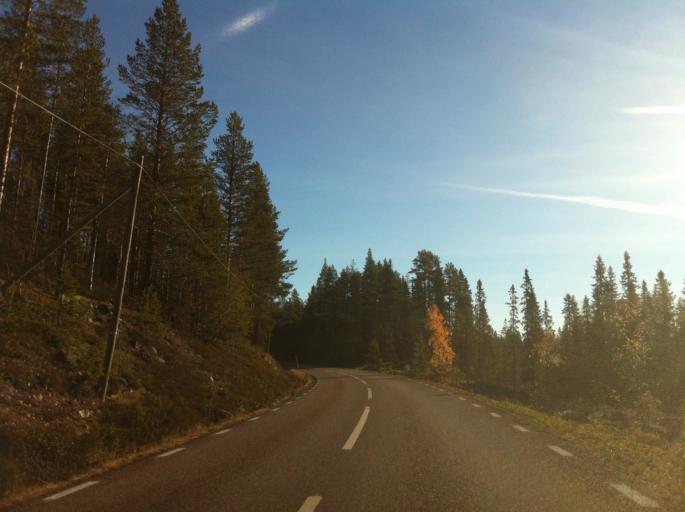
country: NO
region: Hedmark
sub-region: Trysil
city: Innbygda
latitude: 61.8279
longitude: 12.8686
